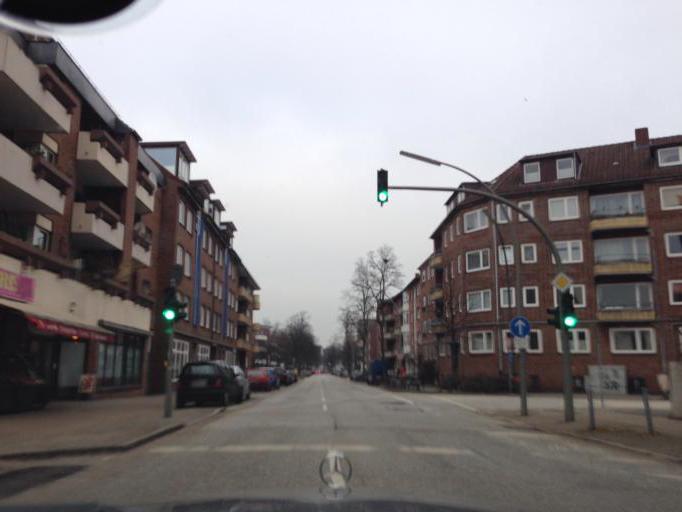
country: DE
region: Hamburg
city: Borgfelde
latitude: 53.5687
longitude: 10.0438
